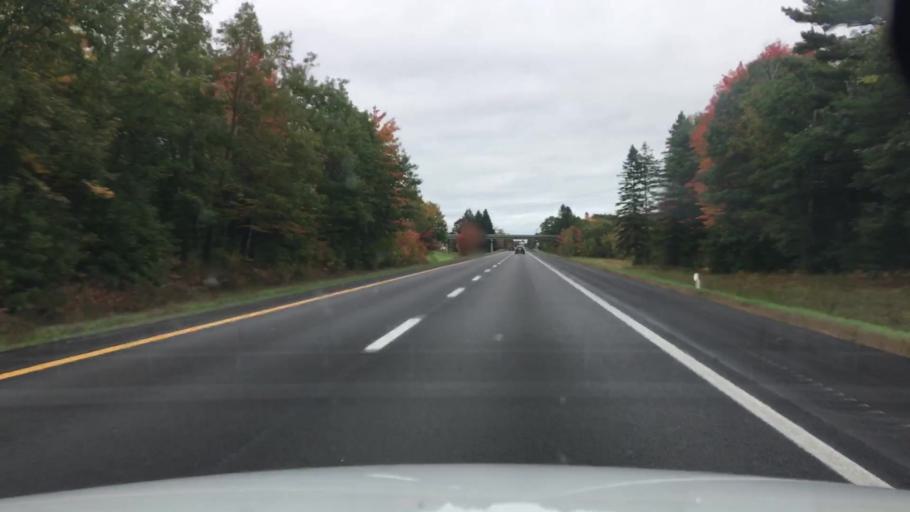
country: US
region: Maine
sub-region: Penobscot County
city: Veazie
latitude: 44.8428
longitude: -68.7329
